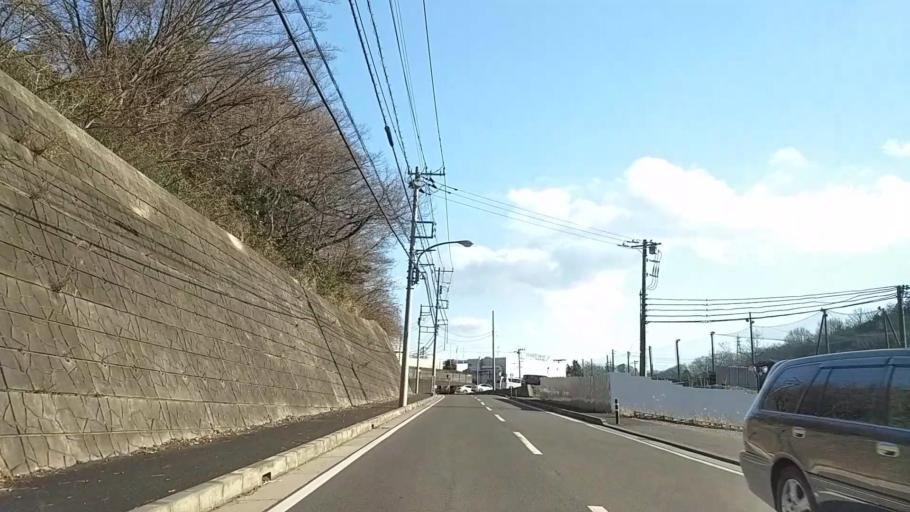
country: JP
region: Kanagawa
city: Atsugi
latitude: 35.4584
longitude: 139.3141
